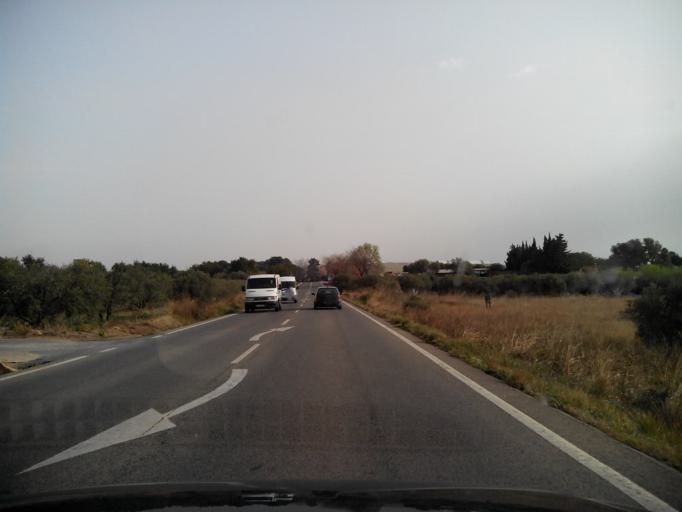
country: ES
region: Catalonia
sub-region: Provincia de Tarragona
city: Riudoms
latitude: 41.1111
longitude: 1.0905
